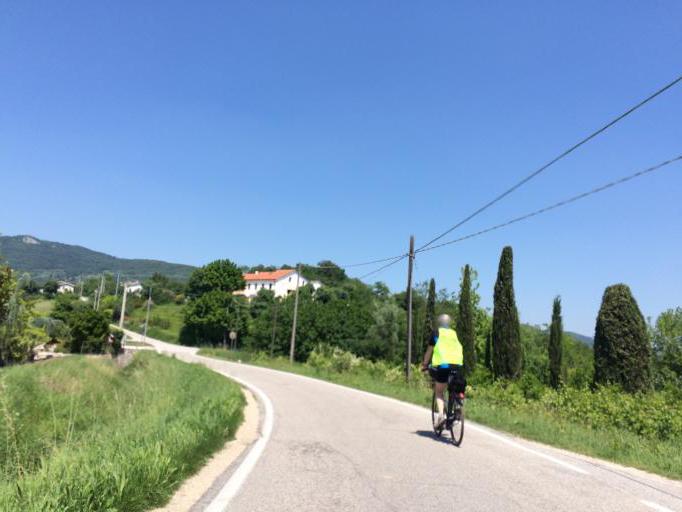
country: IT
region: Veneto
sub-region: Provincia di Vicenza
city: Barbarano Vicentino
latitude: 45.3998
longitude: 11.5546
